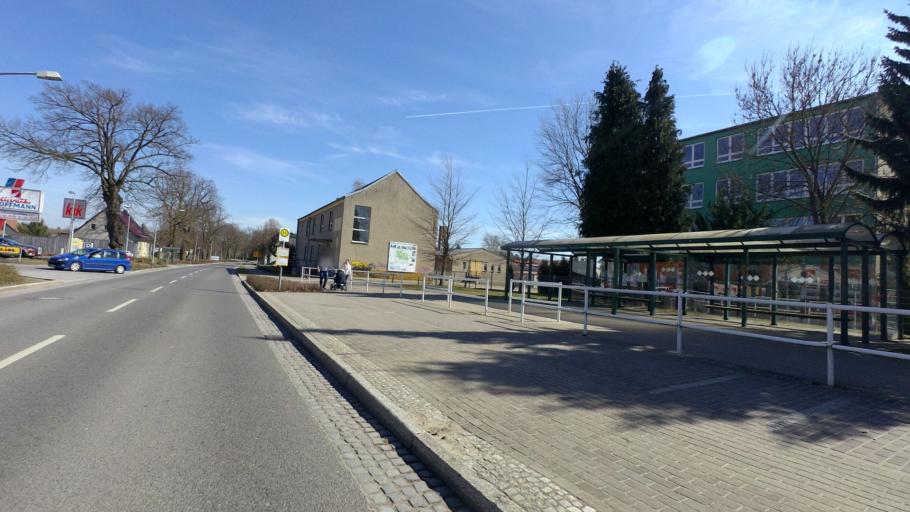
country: DE
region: Brandenburg
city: Muncheberg
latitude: 52.5015
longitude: 14.1461
